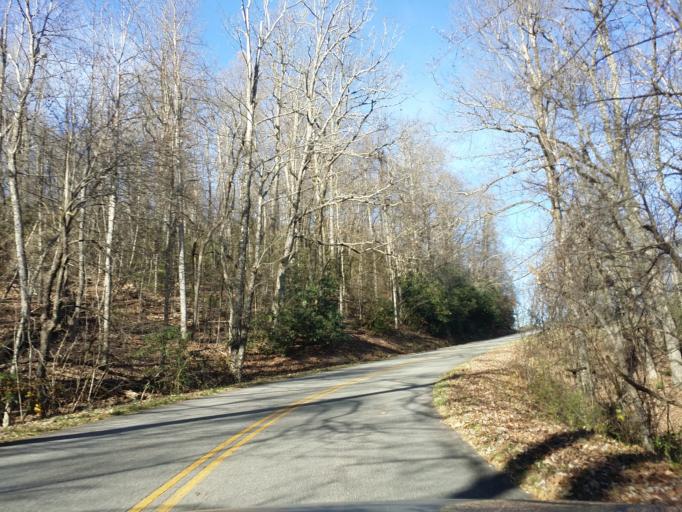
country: US
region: North Carolina
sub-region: McDowell County
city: West Marion
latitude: 35.7554
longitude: -82.1820
